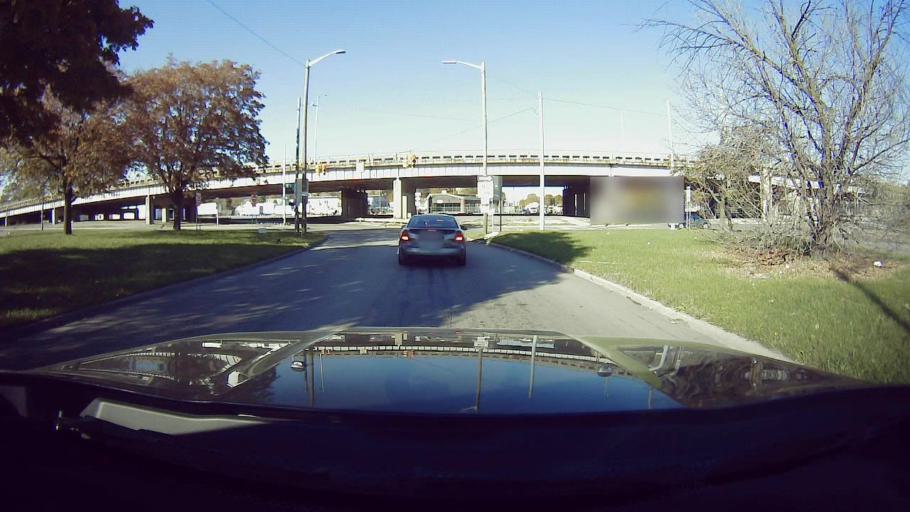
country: US
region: Michigan
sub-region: Oakland County
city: Hazel Park
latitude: 42.4464
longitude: -83.0956
